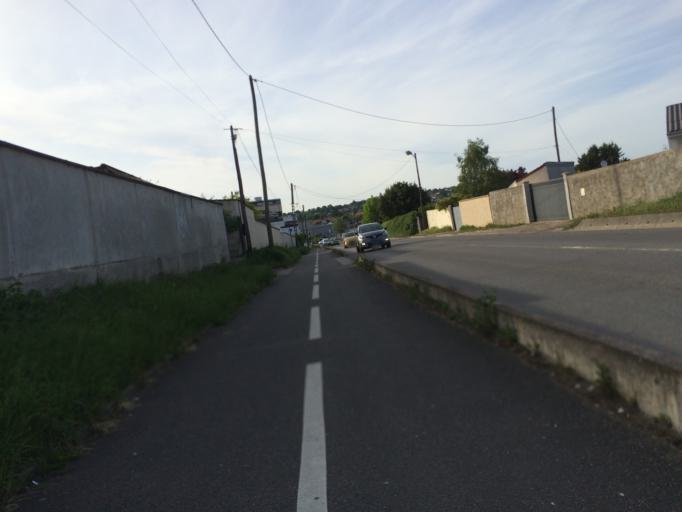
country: FR
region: Ile-de-France
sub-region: Departement de l'Essonne
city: La Ville-du-Bois
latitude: 48.6495
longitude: 2.2758
